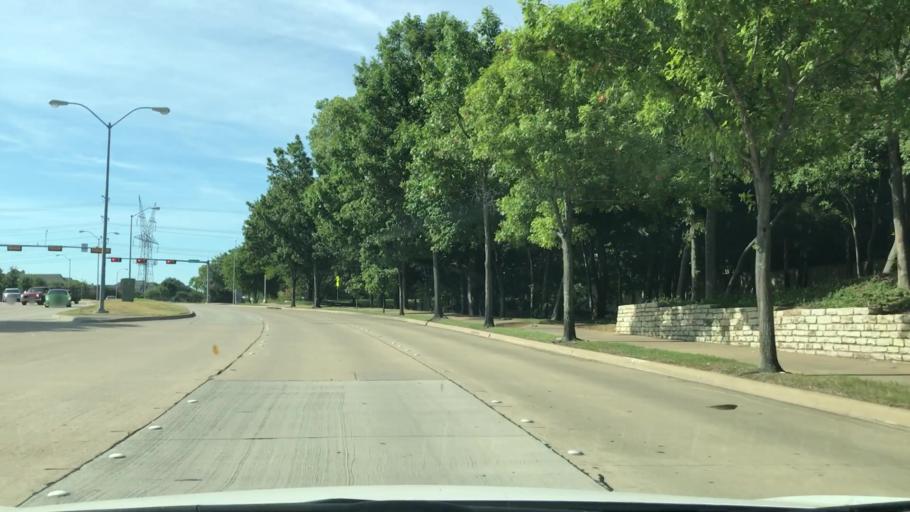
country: US
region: Texas
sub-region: Denton County
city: The Colony
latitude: 33.0622
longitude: -96.8395
